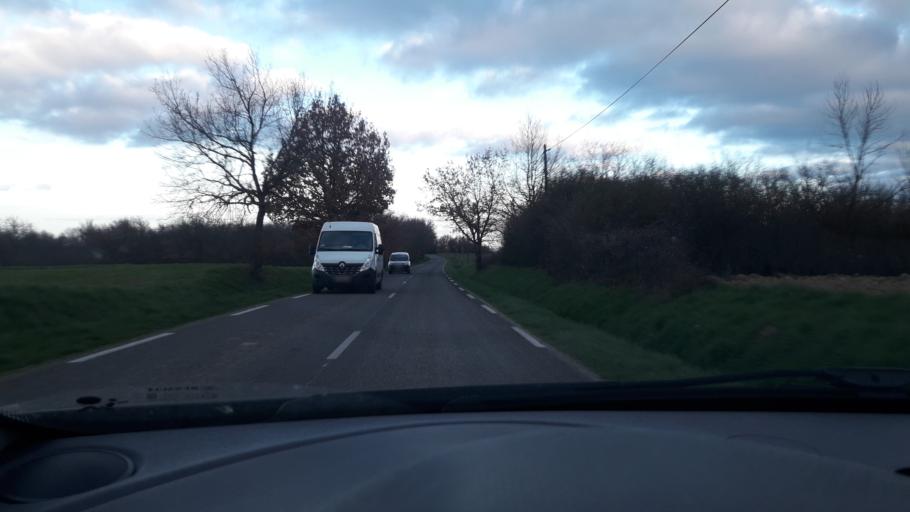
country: FR
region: Midi-Pyrenees
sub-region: Departement de la Haute-Garonne
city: Launac
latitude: 43.7432
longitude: 1.1310
